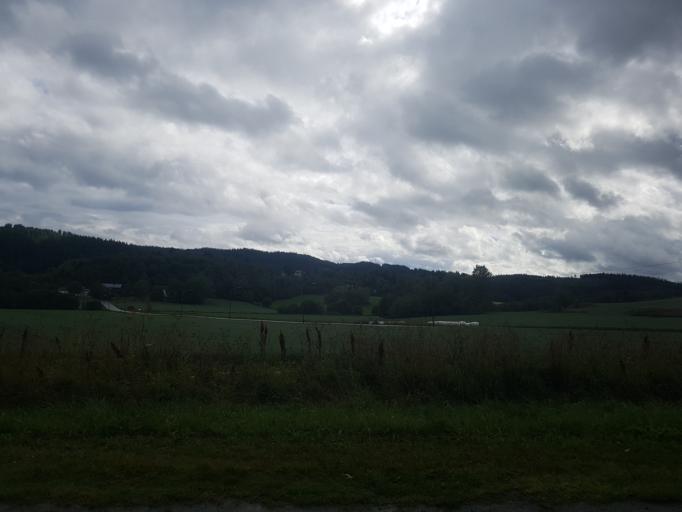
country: NO
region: Sor-Trondelag
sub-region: Trondheim
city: Trondheim
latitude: 63.4057
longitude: 10.4652
